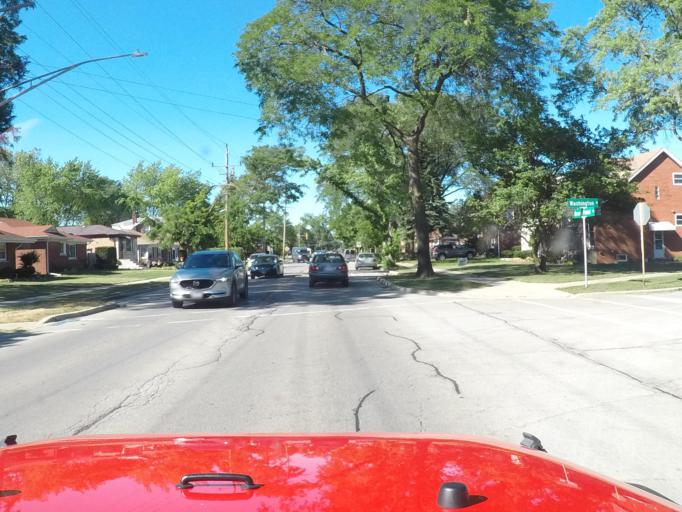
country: US
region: Illinois
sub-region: Cook County
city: Morton Grove
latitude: 42.0328
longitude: -87.7625
